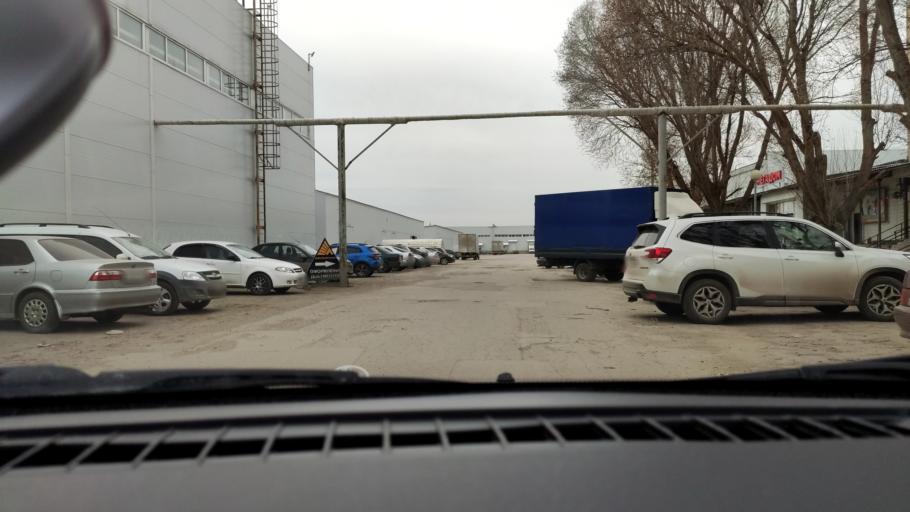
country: RU
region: Samara
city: Smyshlyayevka
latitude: 53.2572
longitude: 50.3705
